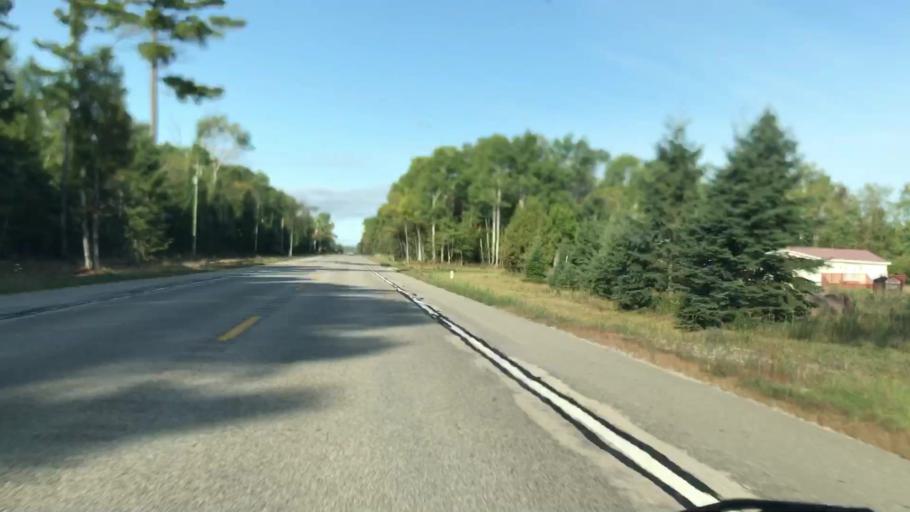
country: US
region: Michigan
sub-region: Luce County
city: Newberry
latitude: 46.3035
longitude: -85.3538
